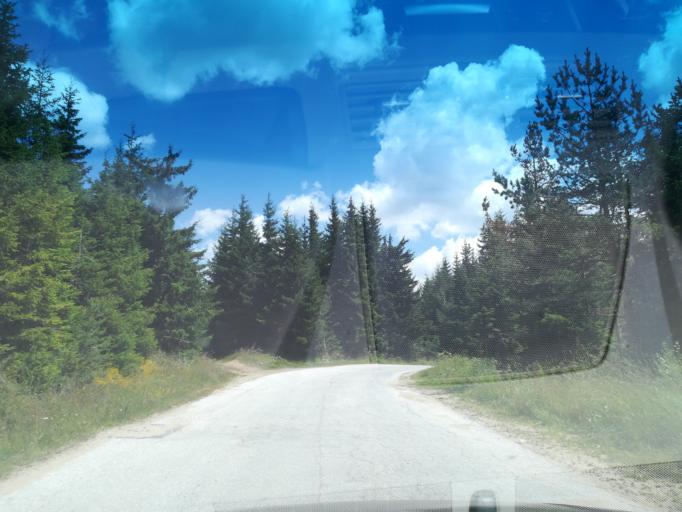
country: BG
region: Smolyan
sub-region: Obshtina Chepelare
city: Chepelare
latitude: 41.6947
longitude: 24.7803
